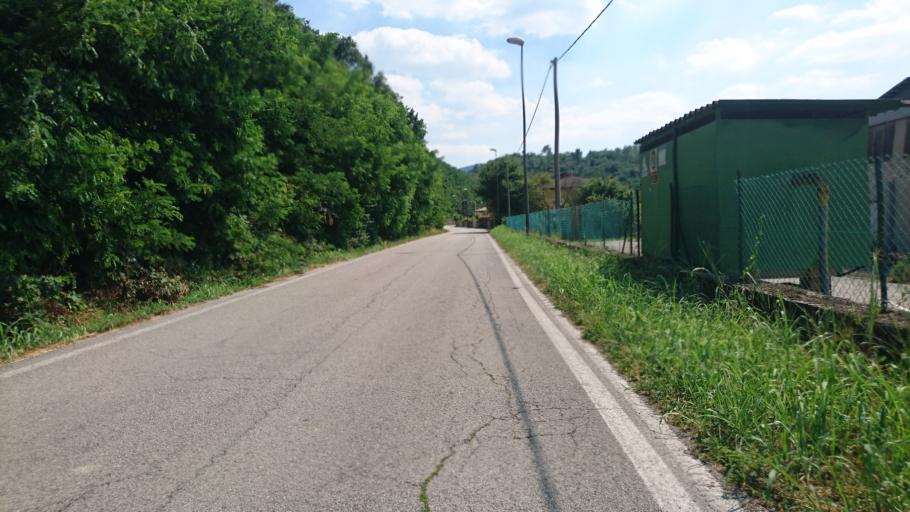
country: IT
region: Veneto
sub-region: Provincia di Padova
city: Treponti
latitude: 45.3640
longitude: 11.7060
